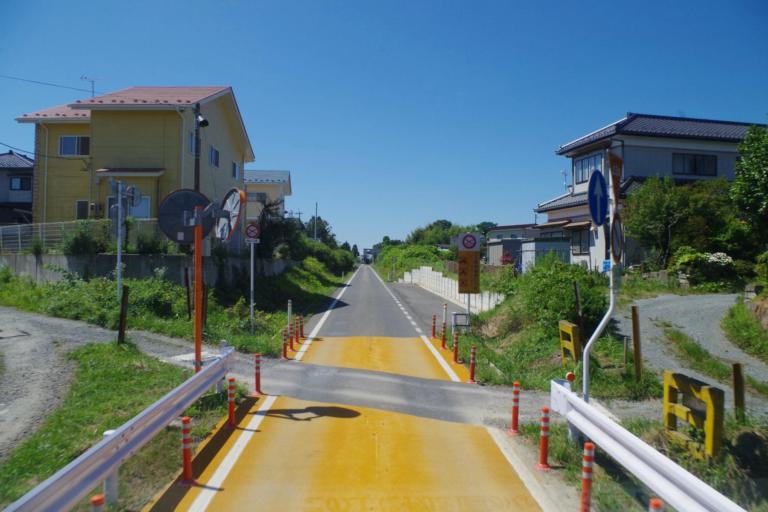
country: JP
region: Iwate
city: Ofunato
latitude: 38.8403
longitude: 141.5811
